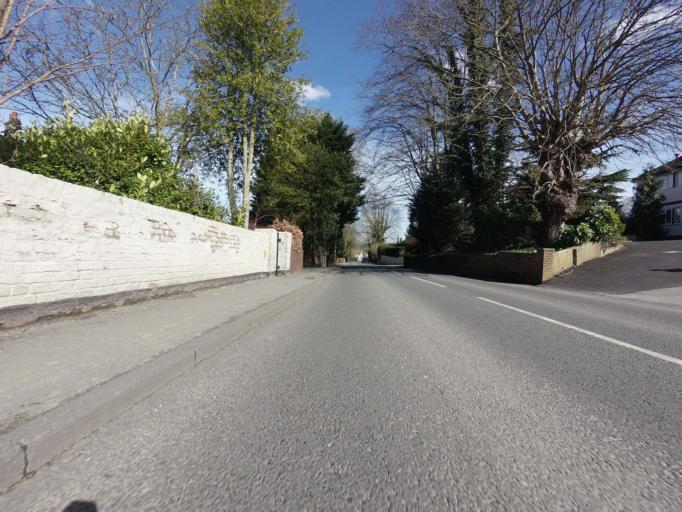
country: GB
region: England
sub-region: Kent
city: Eynsford
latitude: 51.3654
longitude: 0.2067
